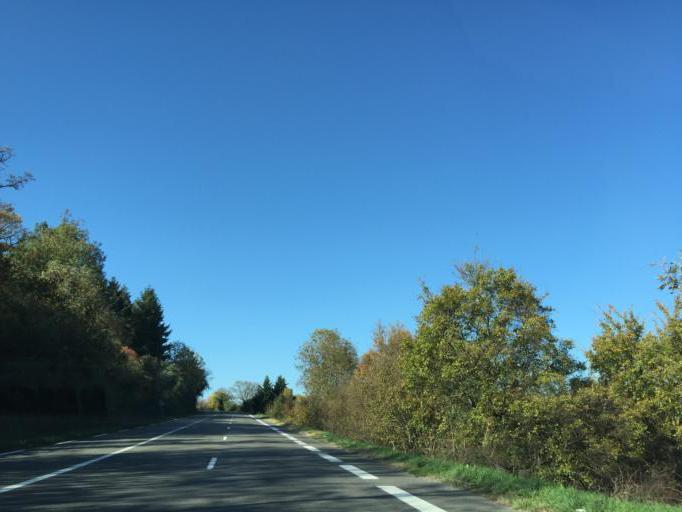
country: FR
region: Rhone-Alpes
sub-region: Departement du Rhone
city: Montagny
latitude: 45.6424
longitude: 4.7482
